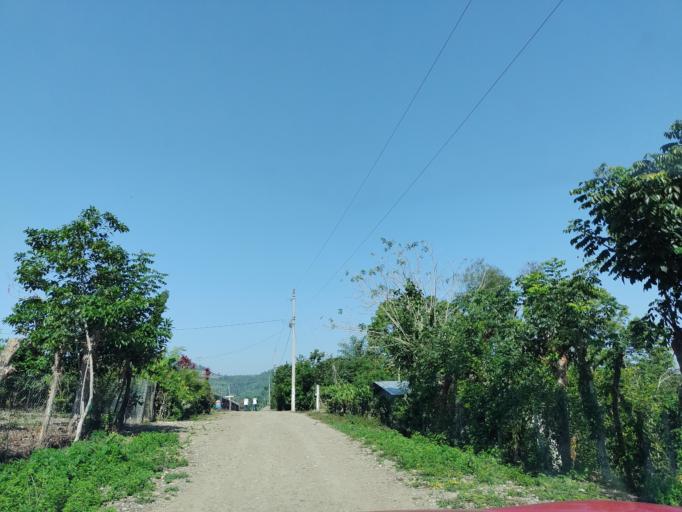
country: MX
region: Veracruz
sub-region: Papantla
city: Polutla
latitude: 20.5152
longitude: -97.2422
